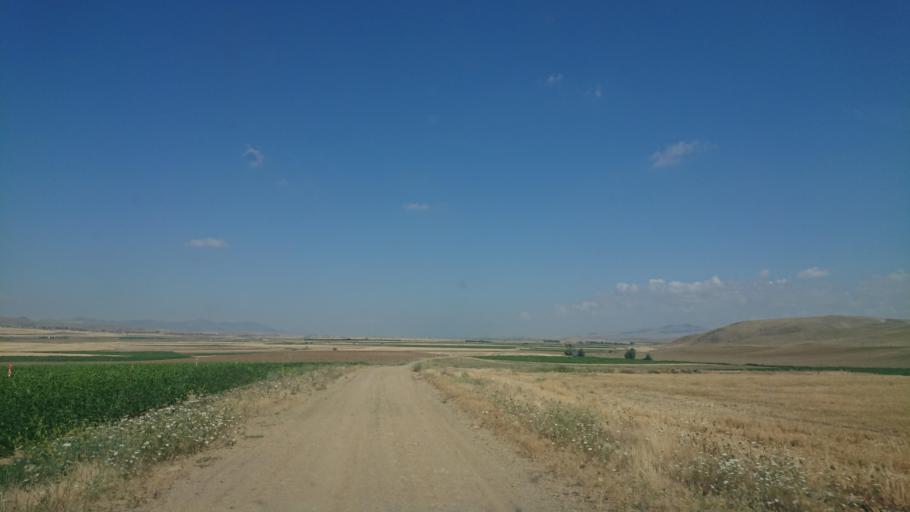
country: TR
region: Aksaray
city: Sariyahsi
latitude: 38.9674
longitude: 33.9221
